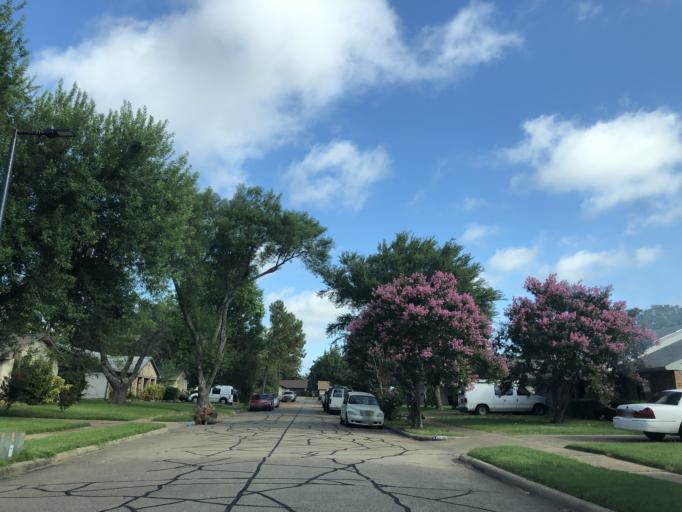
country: US
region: Texas
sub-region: Dallas County
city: Garland
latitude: 32.8585
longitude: -96.6355
